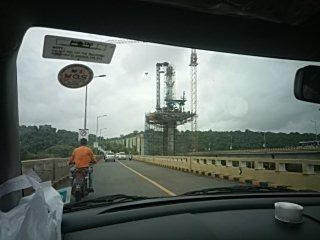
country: IN
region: Goa
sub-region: North Goa
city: Panaji
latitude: 15.5035
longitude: 73.8364
